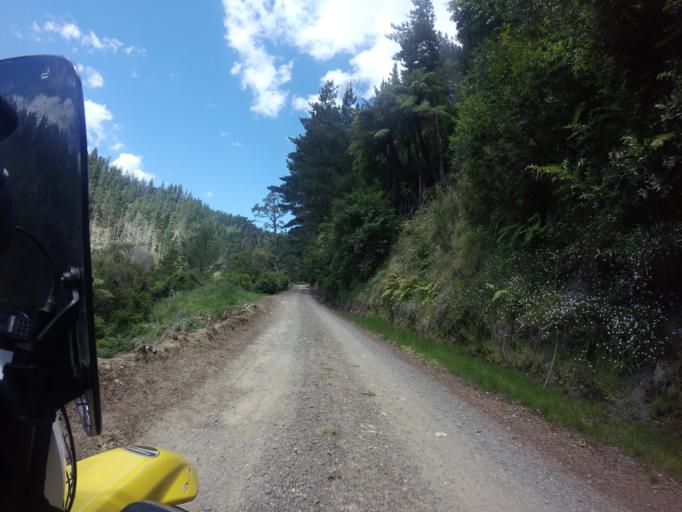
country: NZ
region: Hawke's Bay
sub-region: Wairoa District
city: Wairoa
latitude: -38.9723
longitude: 177.6856
